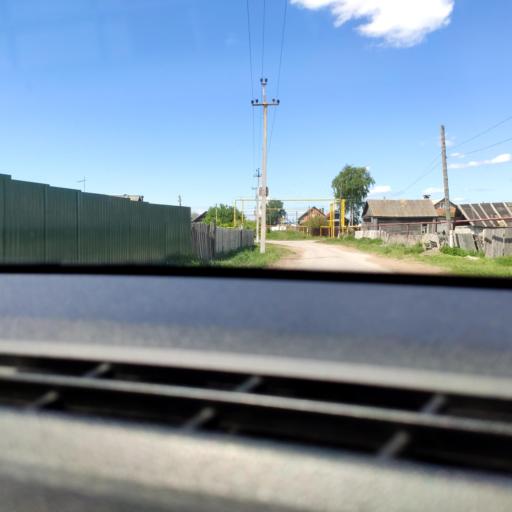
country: RU
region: Samara
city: Povolzhskiy
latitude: 53.6446
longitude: 49.6974
